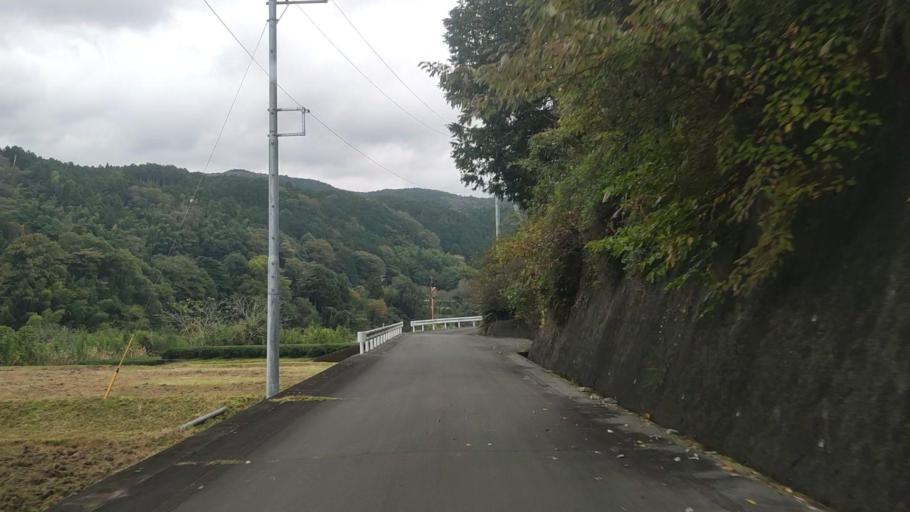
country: JP
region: Shizuoka
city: Ito
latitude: 34.9182
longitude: 138.9808
